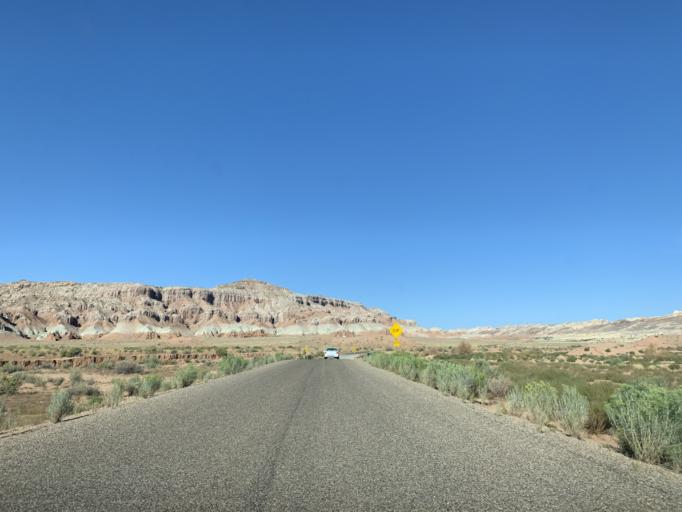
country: US
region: Utah
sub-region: Emery County
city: Ferron
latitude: 38.5750
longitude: -110.7497
